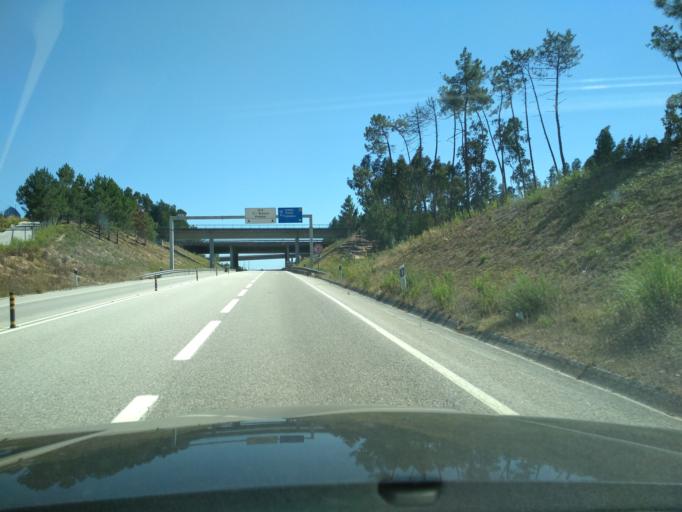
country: PT
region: Leiria
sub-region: Pombal
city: Pombal
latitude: 39.9445
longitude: -8.6770
